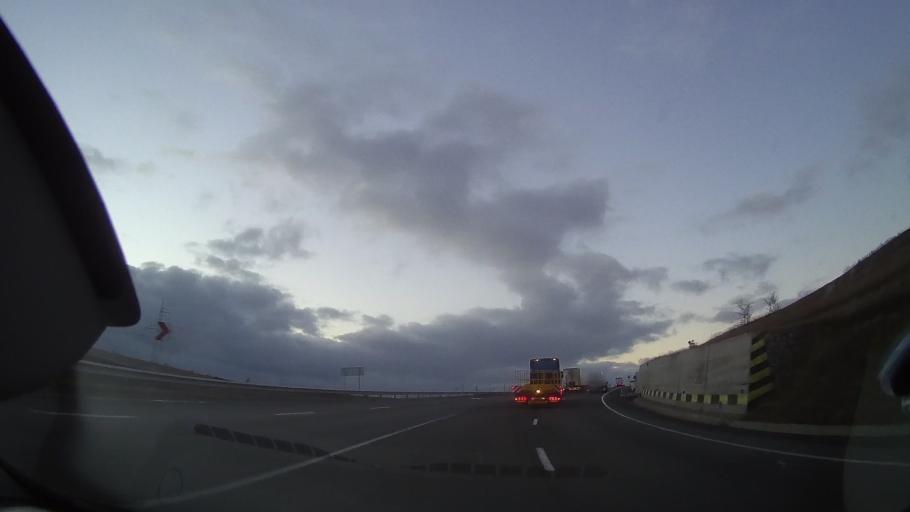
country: RO
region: Cluj
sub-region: Comuna Izvoru Crisului
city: Izvoru Crisului
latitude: 46.8236
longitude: 23.1589
